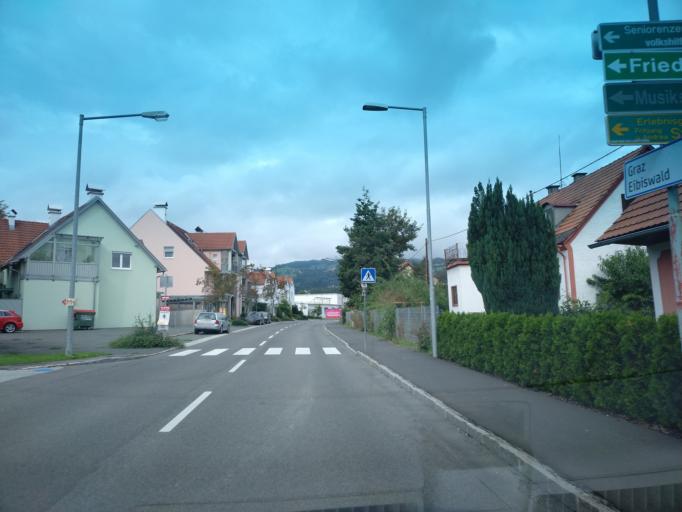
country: AT
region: Styria
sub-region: Politischer Bezirk Deutschlandsberg
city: Deutschlandsberg
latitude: 46.8135
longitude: 15.2237
